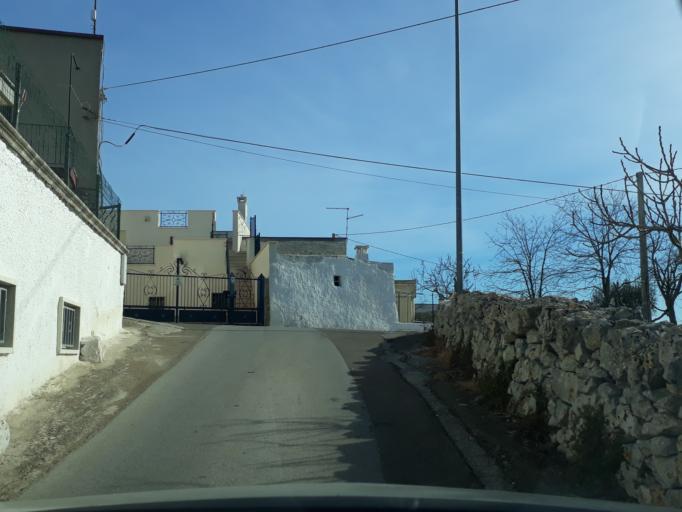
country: IT
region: Apulia
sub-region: Provincia di Brindisi
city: Lamie di Olimpie-Selva
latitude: 40.7897
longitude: 17.3645
